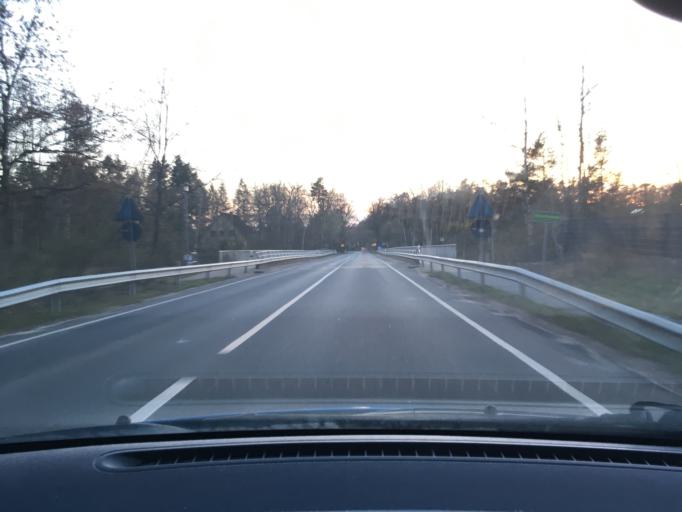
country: DE
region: Lower Saxony
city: Bad Bevensen
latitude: 53.0859
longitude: 10.6003
